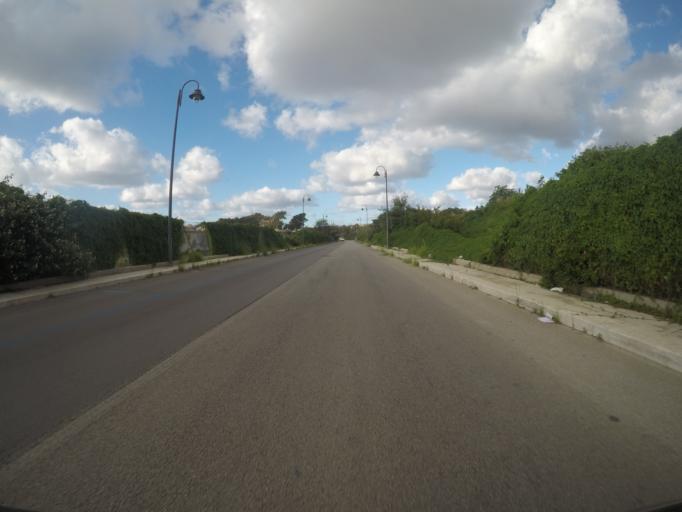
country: IT
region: Sicily
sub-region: Palermo
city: Isola delle Femmine
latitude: 38.1909
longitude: 13.2453
